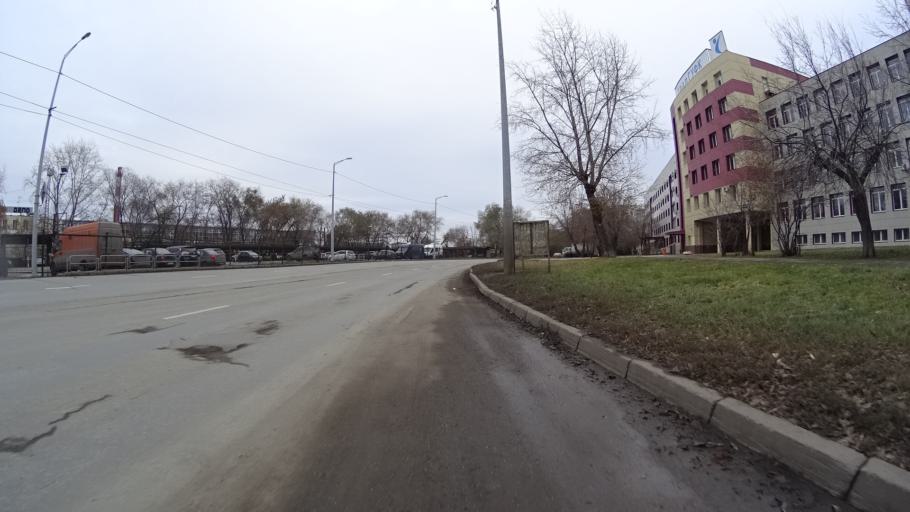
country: RU
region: Chelyabinsk
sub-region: Gorod Chelyabinsk
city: Chelyabinsk
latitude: 55.1539
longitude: 61.4188
